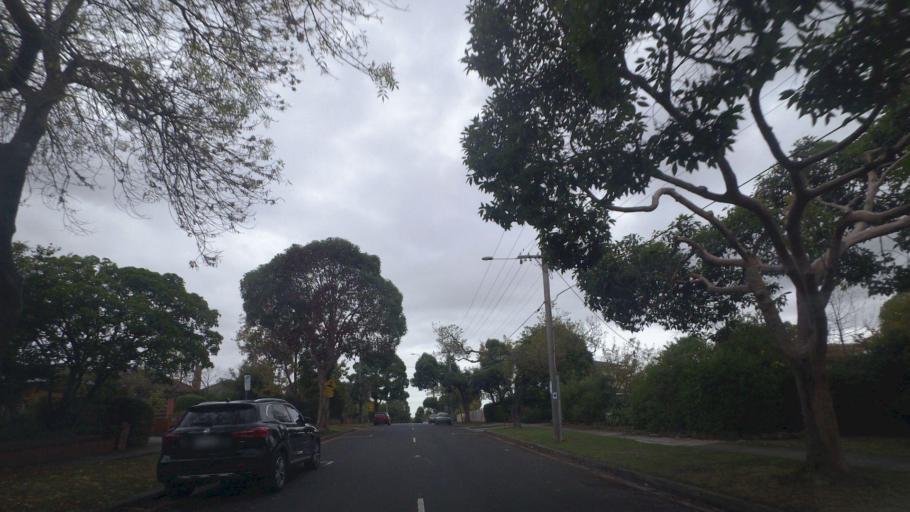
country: AU
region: Victoria
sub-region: Whitehorse
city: Nunawading
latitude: -37.8212
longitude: 145.1787
